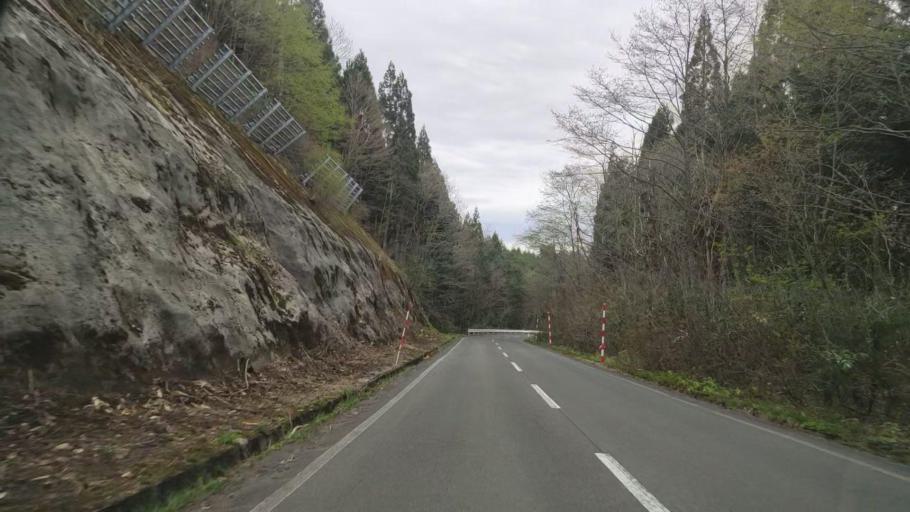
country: JP
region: Akita
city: Hanawa
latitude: 40.3984
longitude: 140.8006
